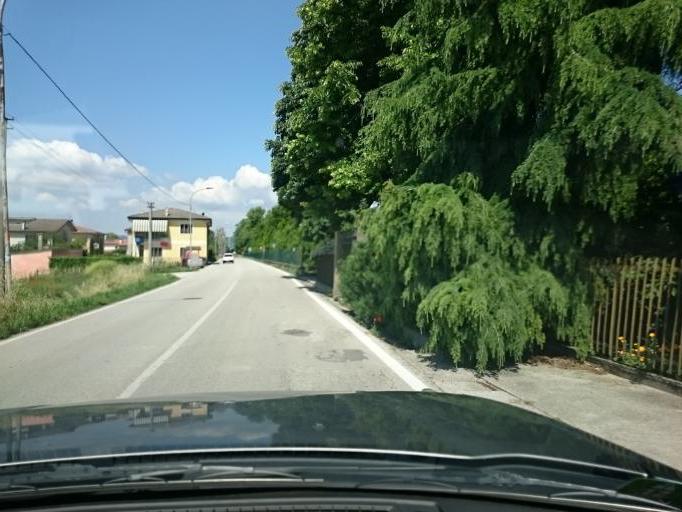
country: IT
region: Veneto
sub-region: Provincia di Vicenza
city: Montegalda
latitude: 45.4478
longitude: 11.6695
